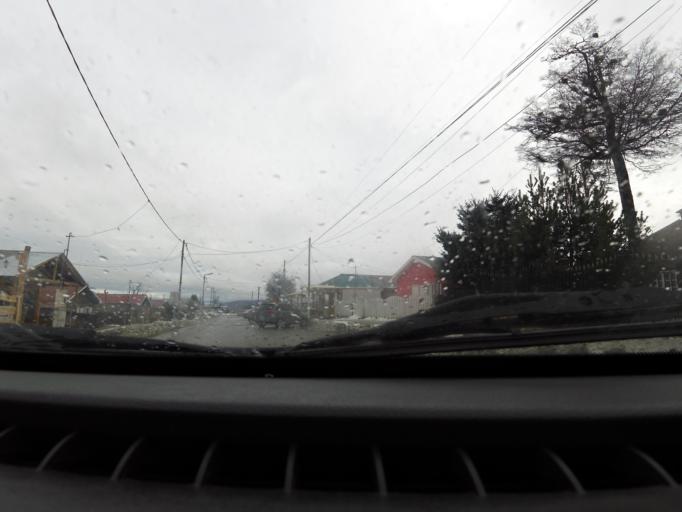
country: AR
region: Tierra del Fuego
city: Rio Grande
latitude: -54.5102
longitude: -67.1978
